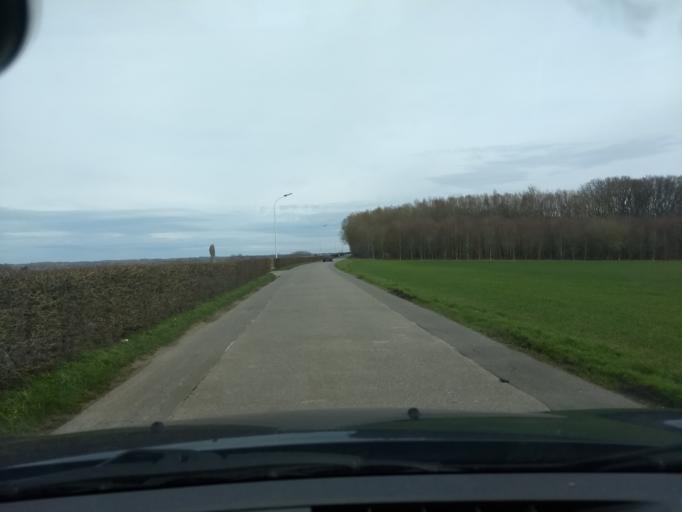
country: BE
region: Flanders
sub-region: Provincie Oost-Vlaanderen
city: Oudenaarde
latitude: 50.9007
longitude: 3.6008
